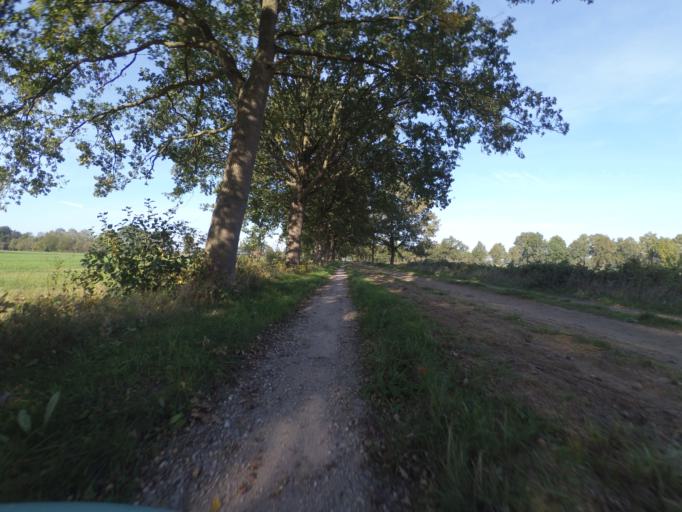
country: NL
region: Gelderland
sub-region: Gemeente Lochem
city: Barchem
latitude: 52.1132
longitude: 6.4036
